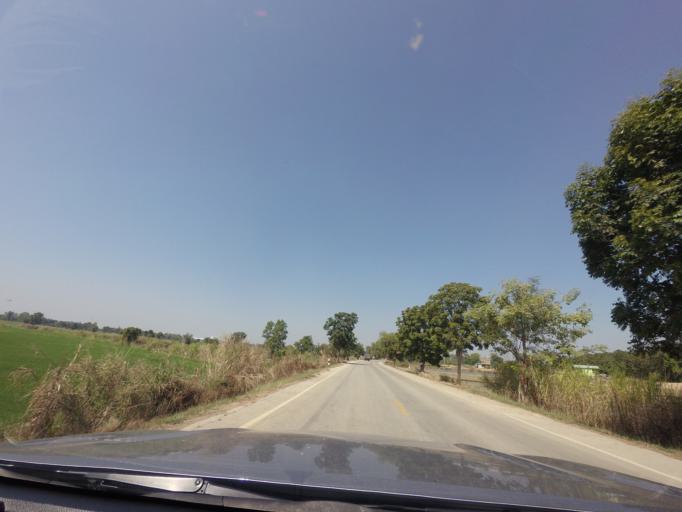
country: TH
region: Sukhothai
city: Si Samrong
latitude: 17.1086
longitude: 99.7785
